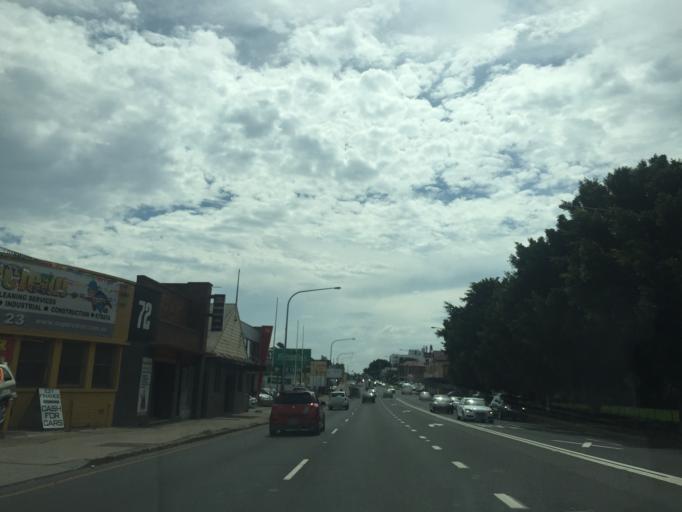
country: AU
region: New South Wales
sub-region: Parramatta
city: Granville
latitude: -33.8324
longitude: 151.0161
